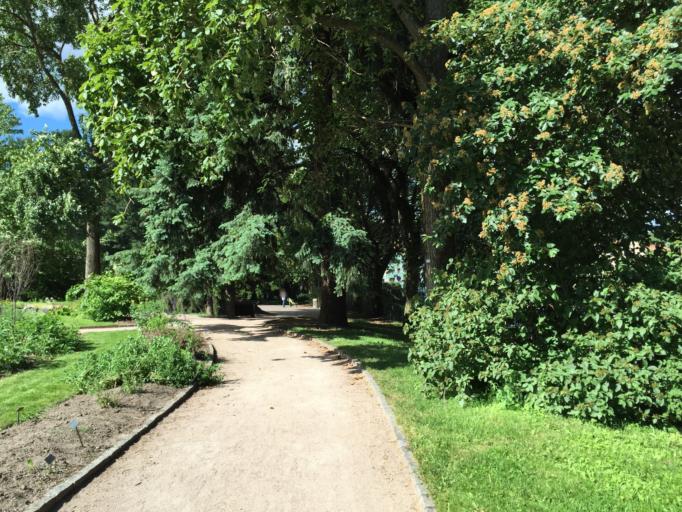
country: NO
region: Oslo
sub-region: Oslo
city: Oslo
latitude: 59.9185
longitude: 10.7729
